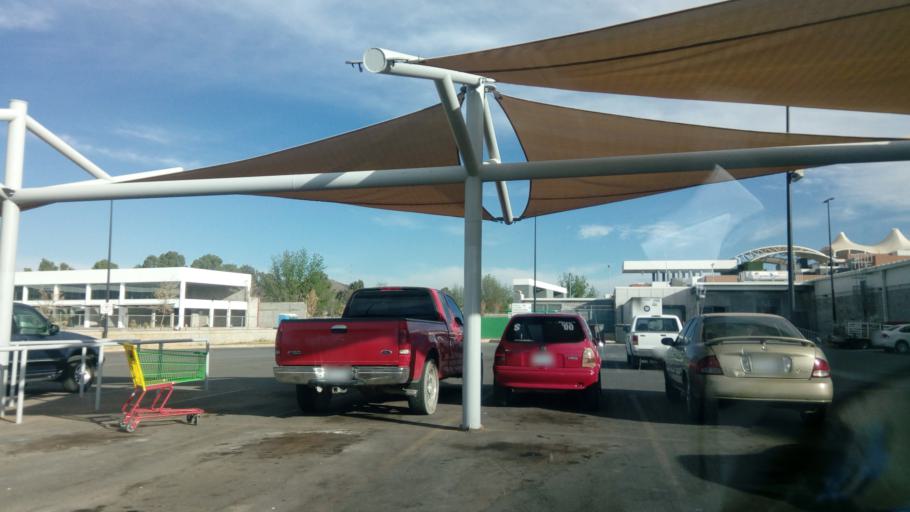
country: MX
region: Durango
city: Victoria de Durango
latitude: 24.0545
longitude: -104.6431
